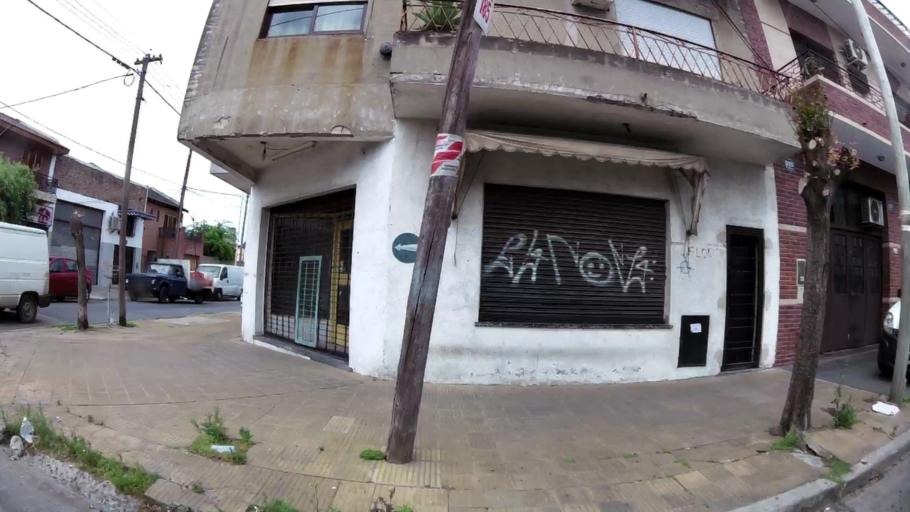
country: AR
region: Buenos Aires F.D.
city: Villa Lugano
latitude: -34.6840
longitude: -58.4961
